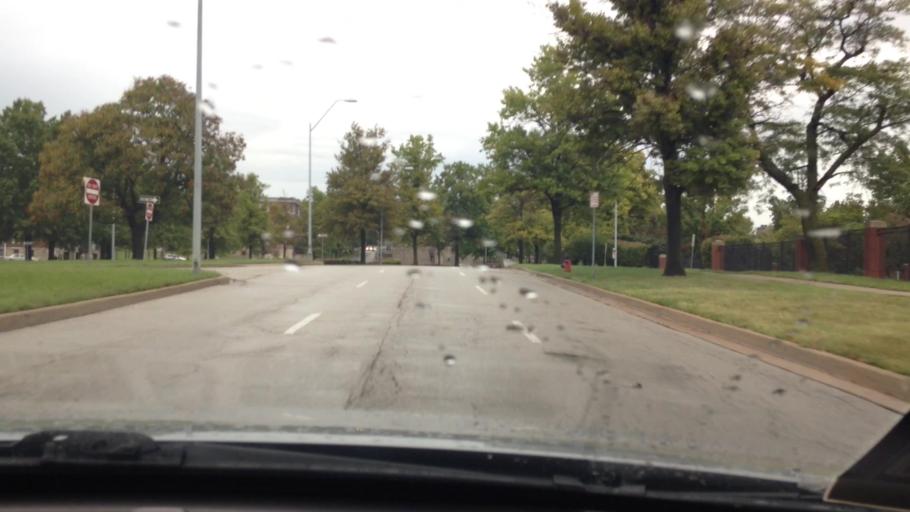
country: US
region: Missouri
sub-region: Jackson County
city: Kansas City
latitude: 39.0975
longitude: -94.5639
